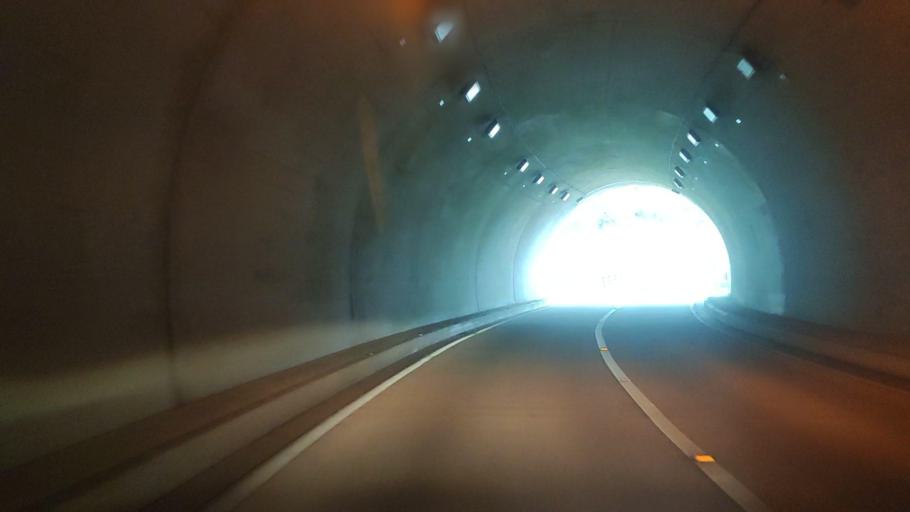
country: JP
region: Nagasaki
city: Shimabara
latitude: 32.7613
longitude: 130.2779
